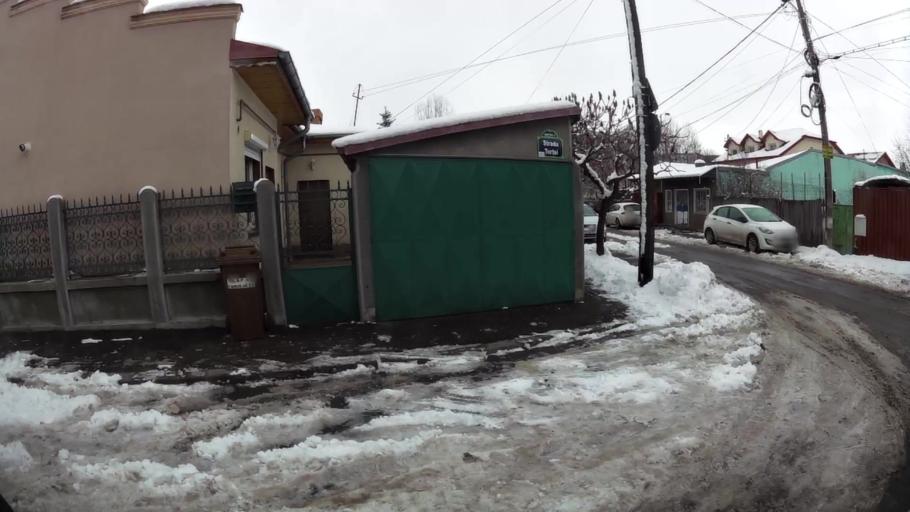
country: RO
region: Bucuresti
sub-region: Municipiul Bucuresti
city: Bucuresti
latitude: 44.3890
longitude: 26.1000
